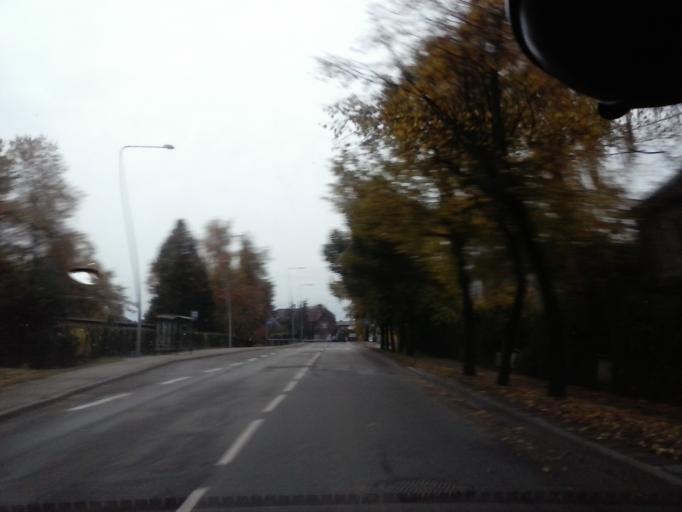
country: EE
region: Tartu
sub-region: Tartu linn
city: Tartu
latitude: 58.3721
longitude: 26.7004
